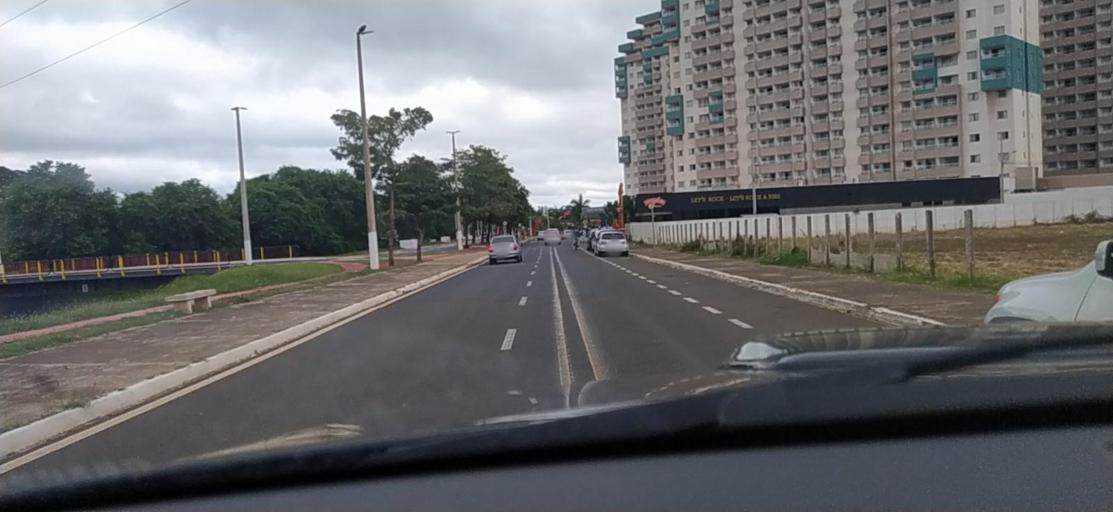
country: BR
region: Sao Paulo
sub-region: Olimpia
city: Olimpia
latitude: -20.7274
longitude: -48.9154
